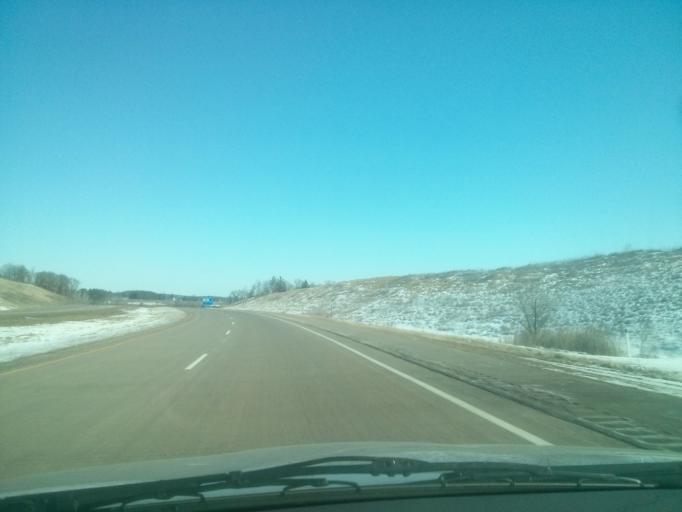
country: US
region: Wisconsin
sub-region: Saint Croix County
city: Somerset
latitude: 45.1110
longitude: -92.6675
